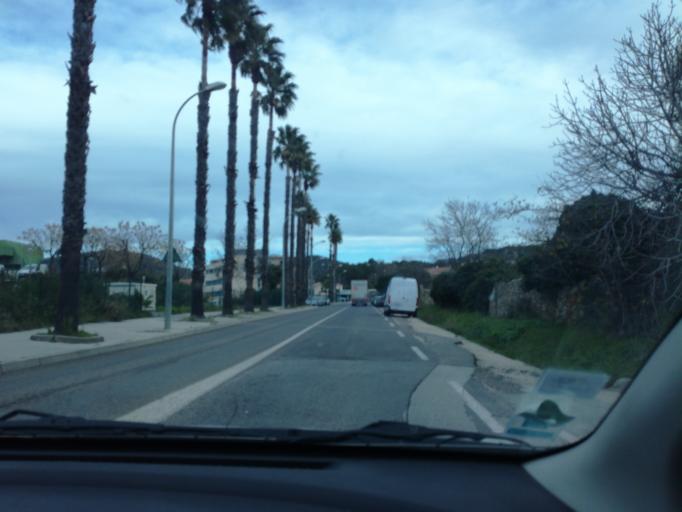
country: FR
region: Provence-Alpes-Cote d'Azur
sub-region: Departement du Var
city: Hyeres
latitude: 43.1183
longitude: 6.1134
